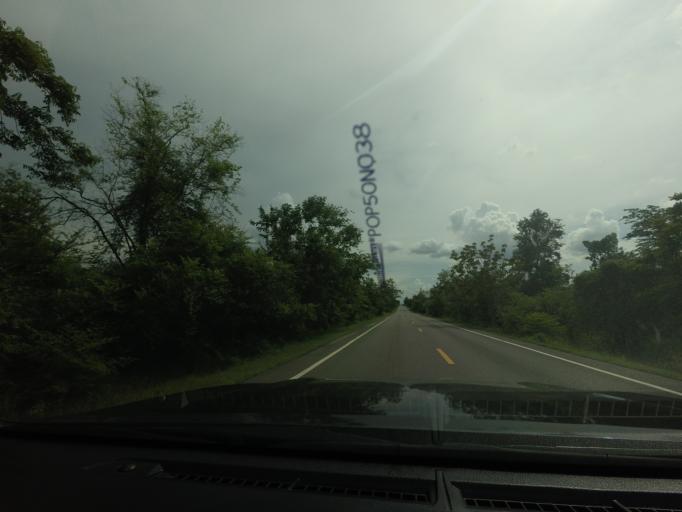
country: TH
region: Kanchanaburi
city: Kanchanaburi
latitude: 14.1533
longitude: 99.4240
